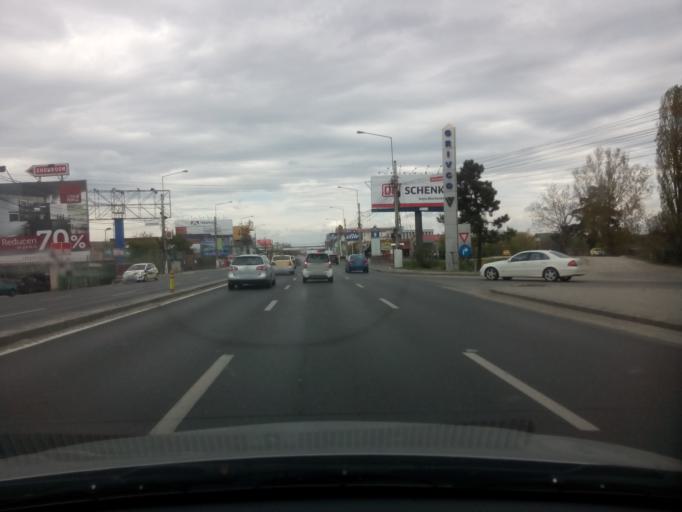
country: RO
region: Ilfov
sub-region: Comuna Otopeni
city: Otopeni
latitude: 44.5382
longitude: 26.0686
